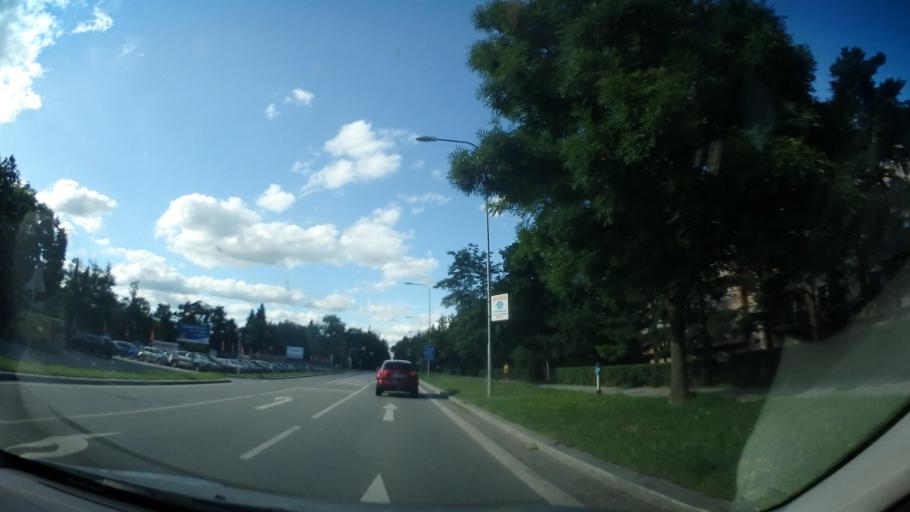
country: CZ
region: South Moravian
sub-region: Okres Blansko
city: Blansko
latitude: 49.3634
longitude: 16.6412
